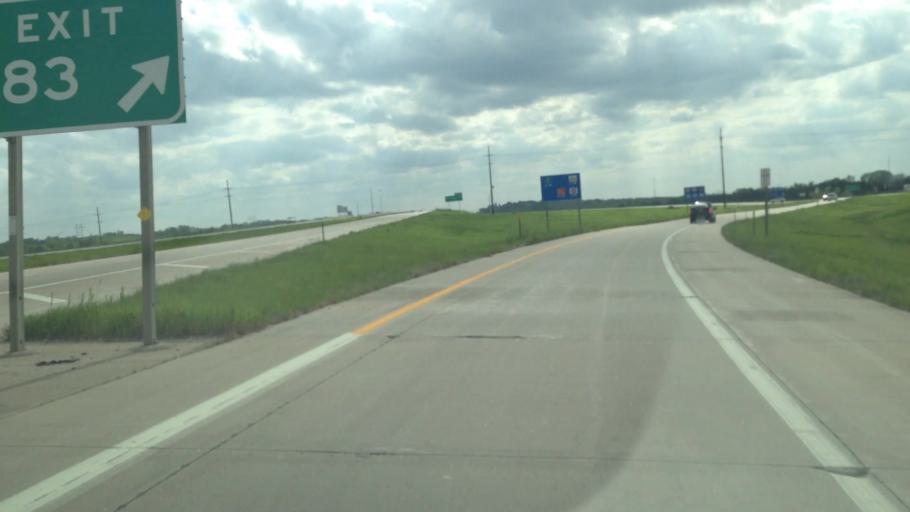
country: US
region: Kansas
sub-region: Franklin County
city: Ottawa
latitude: 38.5769
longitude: -95.2639
